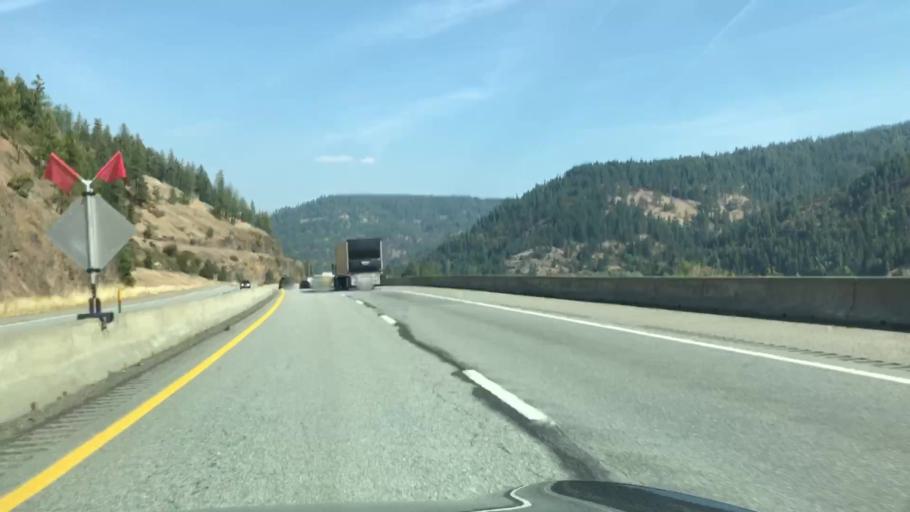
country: US
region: Idaho
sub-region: Kootenai County
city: Coeur d'Alene
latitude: 47.6235
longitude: -116.6612
